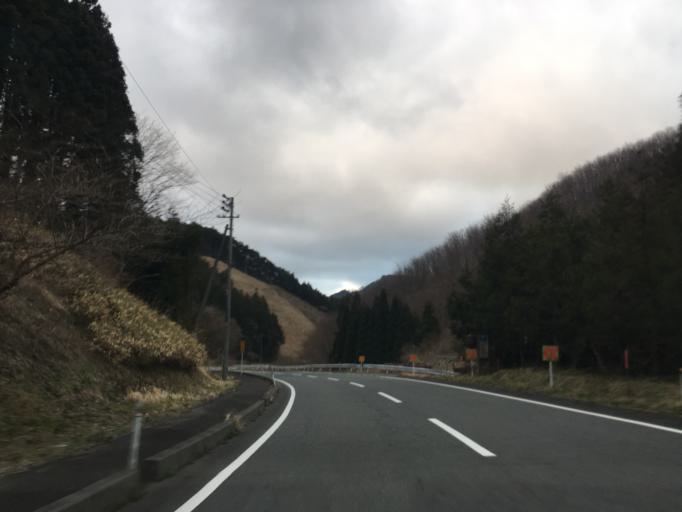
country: JP
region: Ibaraki
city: Kitaibaraki
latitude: 36.9523
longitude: 140.6255
